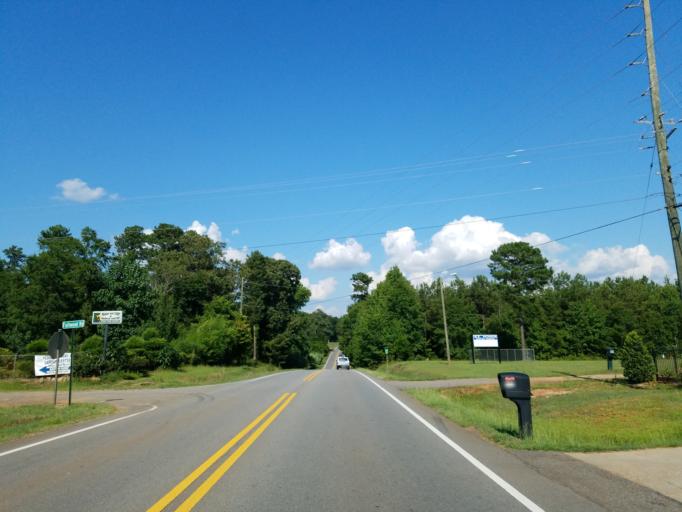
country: US
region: Georgia
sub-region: Peach County
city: Fort Valley
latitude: 32.5568
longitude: -83.8407
